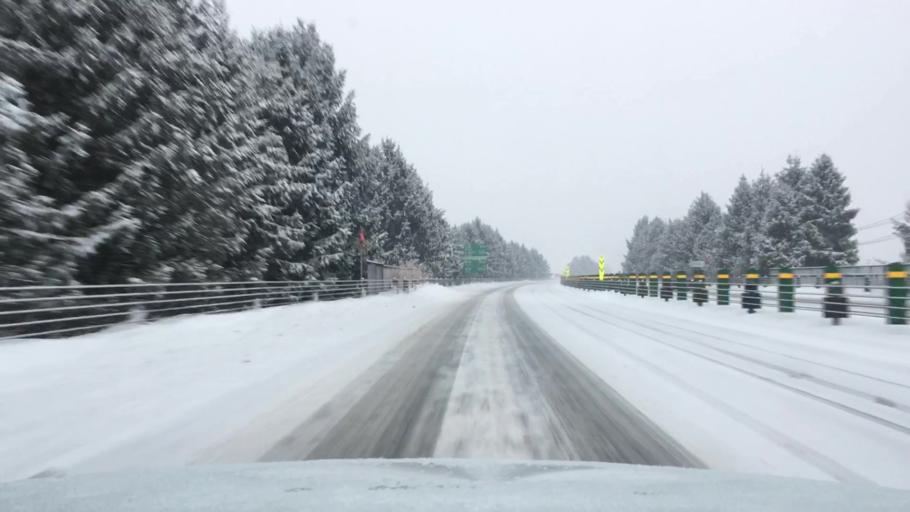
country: JP
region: Akita
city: Hanawa
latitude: 40.2694
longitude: 140.7635
